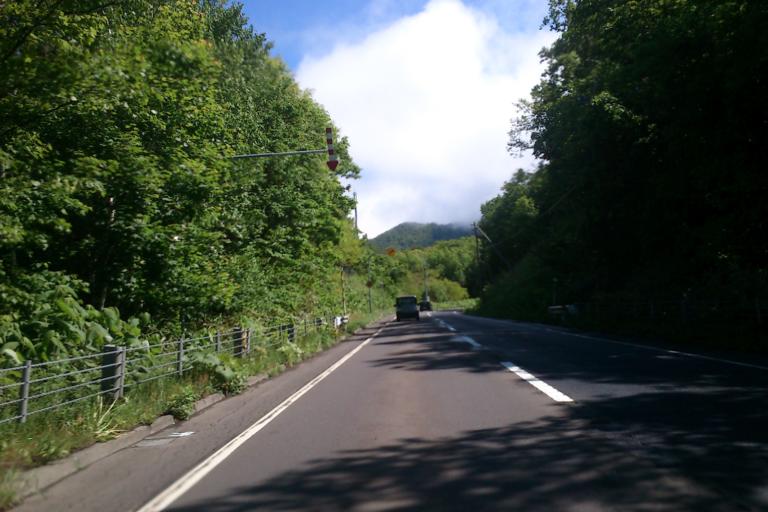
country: JP
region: Hokkaido
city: Ishikari
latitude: 43.5096
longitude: 141.3755
